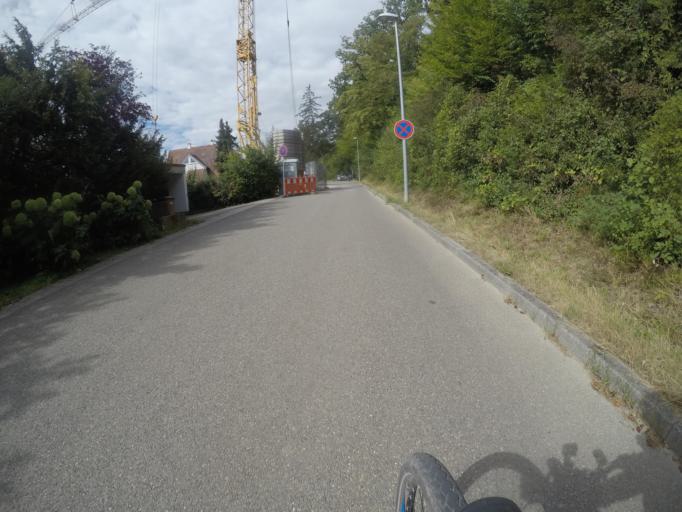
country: DE
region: Baden-Wuerttemberg
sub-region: Regierungsbezirk Stuttgart
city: Stuttgart
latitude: 48.7496
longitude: 9.1204
